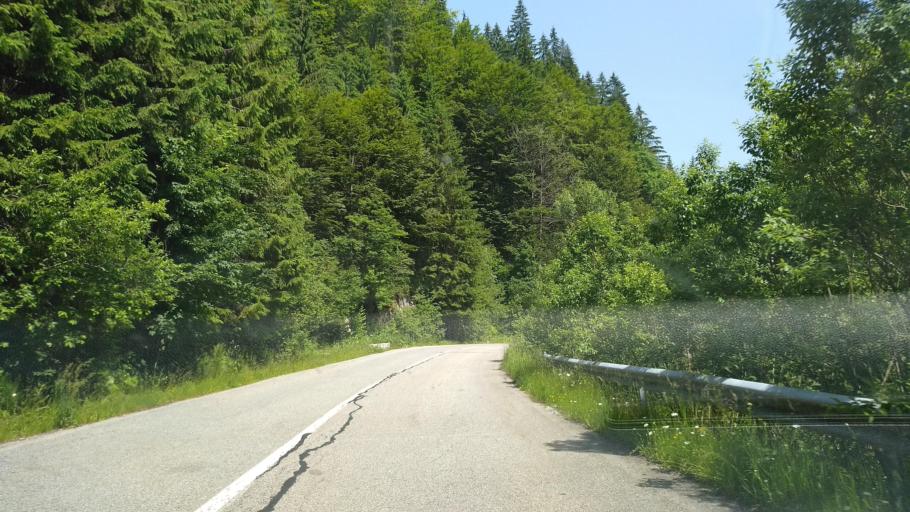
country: RO
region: Gorj
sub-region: Comuna Runcu
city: Valea Mare
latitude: 45.2774
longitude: 22.9354
